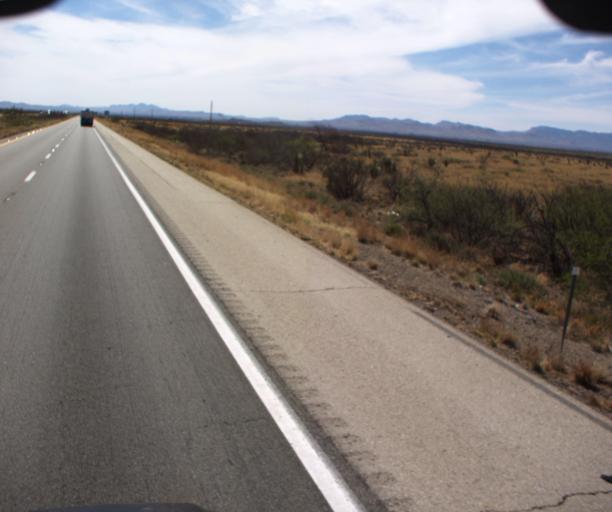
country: US
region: Arizona
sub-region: Cochise County
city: Willcox
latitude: 32.3299
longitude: -109.7692
